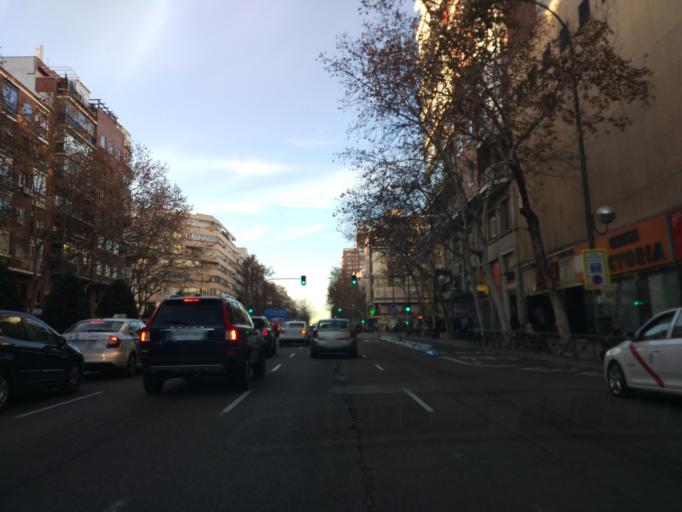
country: ES
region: Madrid
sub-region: Provincia de Madrid
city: Salamanca
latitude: 40.4340
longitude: -3.6737
